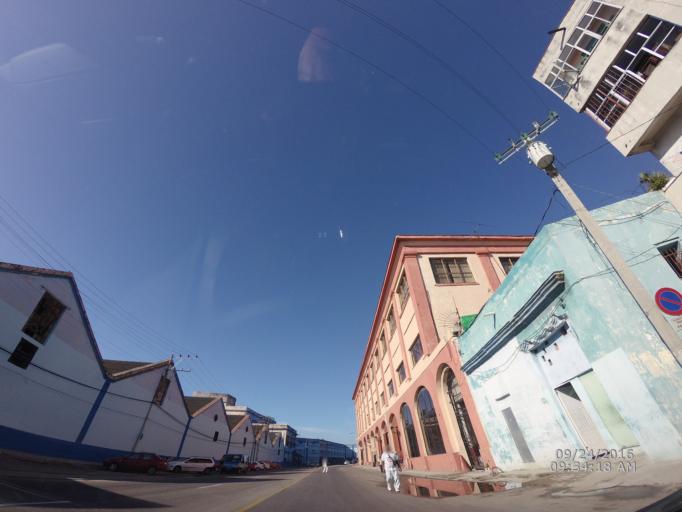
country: CU
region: La Habana
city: La Habana Vieja
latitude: 23.1291
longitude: -82.3507
